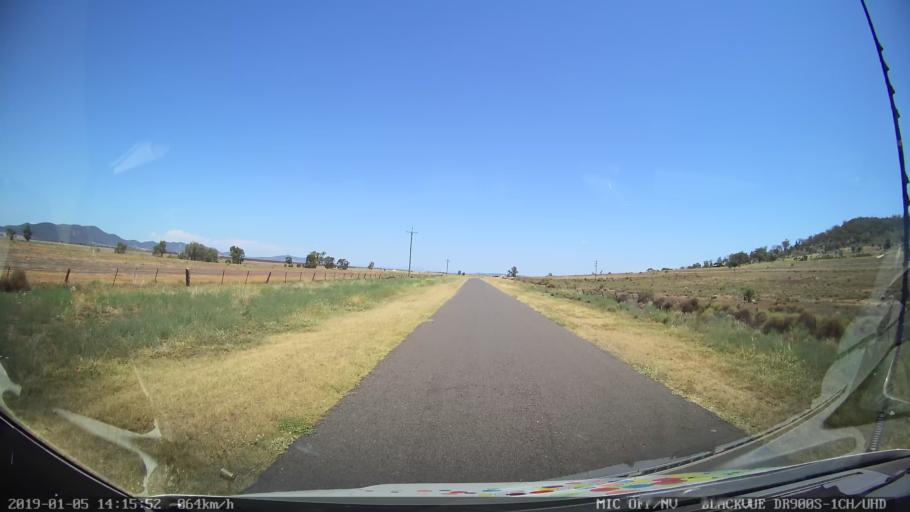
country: AU
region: New South Wales
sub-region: Liverpool Plains
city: Quirindi
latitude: -31.2511
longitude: 150.4717
